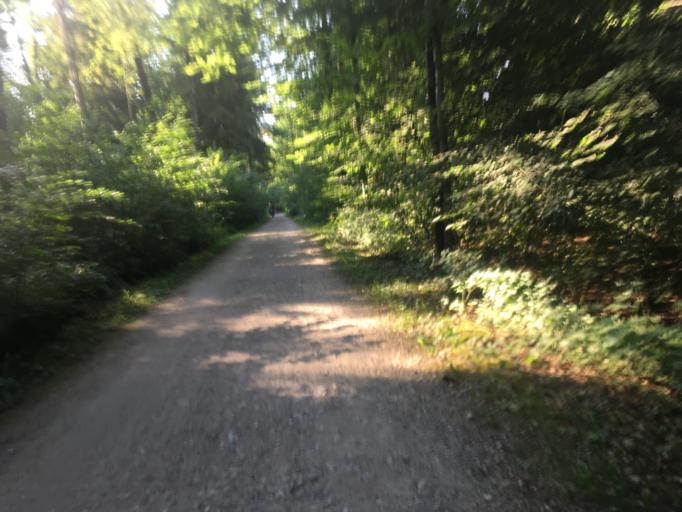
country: CH
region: Bern
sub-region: Emmental District
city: Oberburg
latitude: 47.0297
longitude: 7.6425
